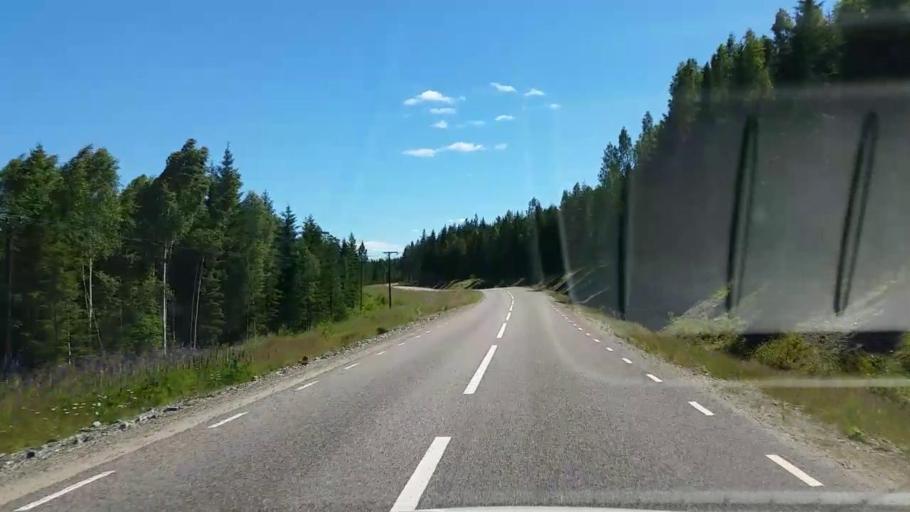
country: SE
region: Gaevleborg
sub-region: Ovanakers Kommun
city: Edsbyn
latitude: 61.5771
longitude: 15.6621
